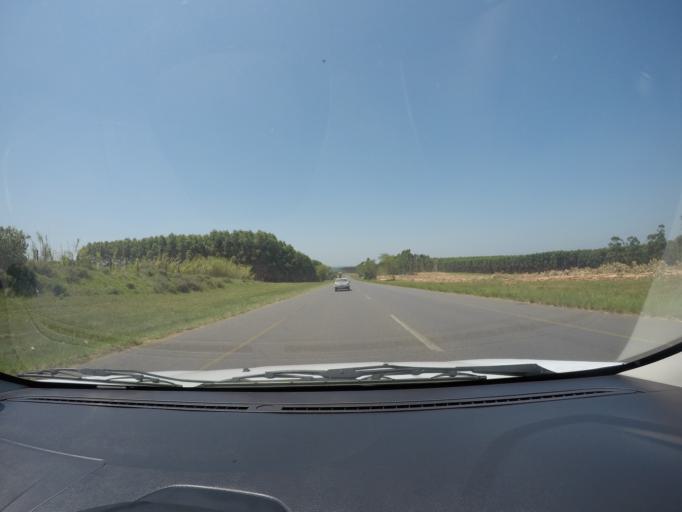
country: ZA
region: KwaZulu-Natal
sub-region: uThungulu District Municipality
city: eSikhawini
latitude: -28.8214
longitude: 31.9490
